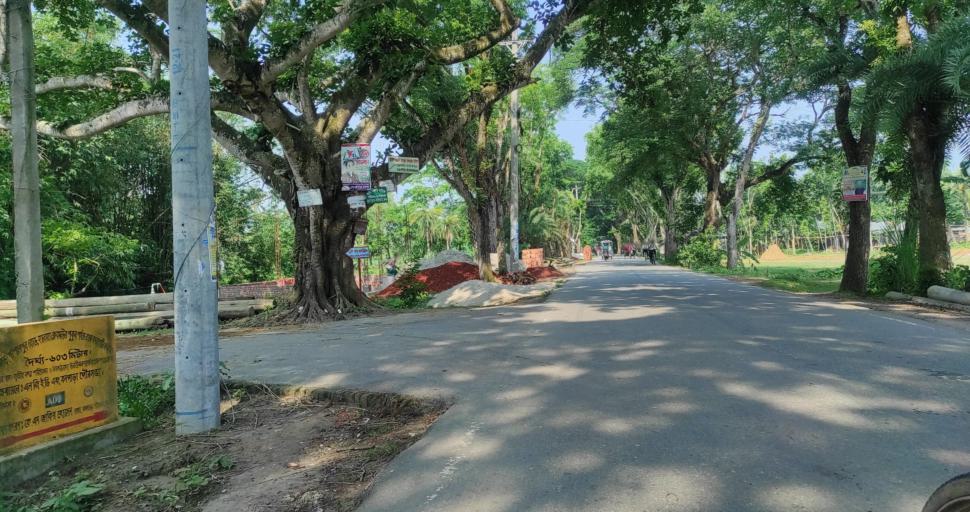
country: BD
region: Rajshahi
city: Ishurdi
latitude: 24.2889
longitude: 89.0734
